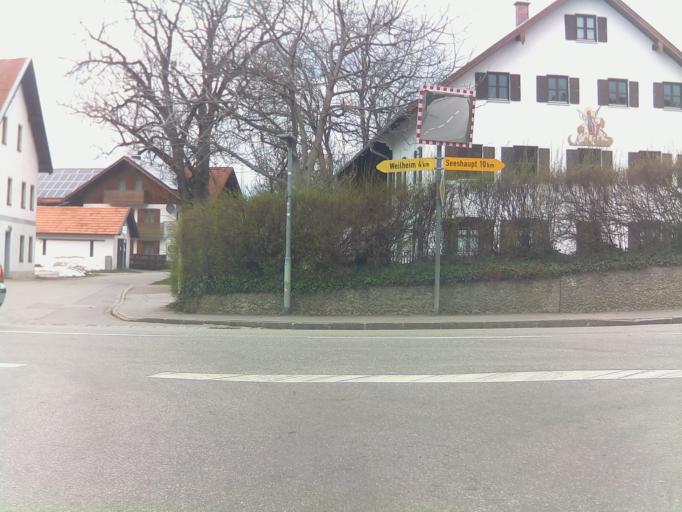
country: DE
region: Bavaria
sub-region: Upper Bavaria
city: Weilheim
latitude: 47.8220
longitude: 11.1898
